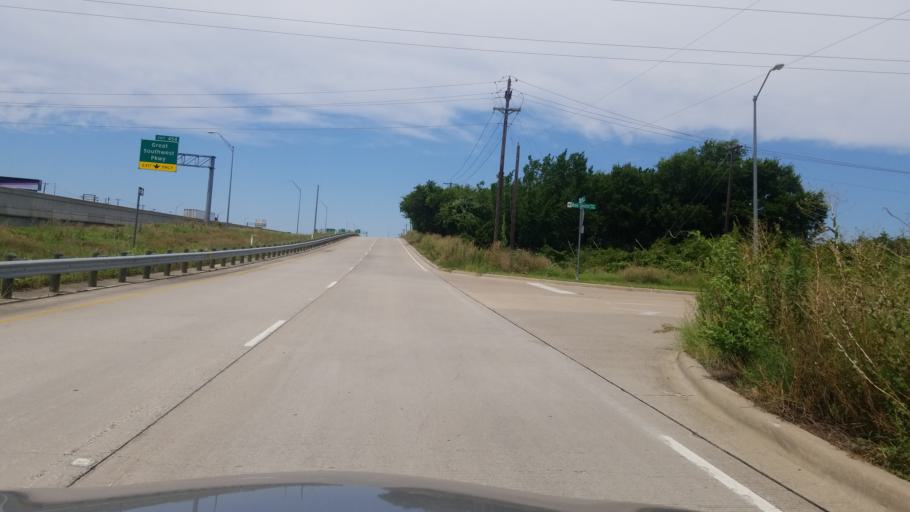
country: US
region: Texas
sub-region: Dallas County
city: Grand Prairie
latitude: 32.6765
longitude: -97.0341
